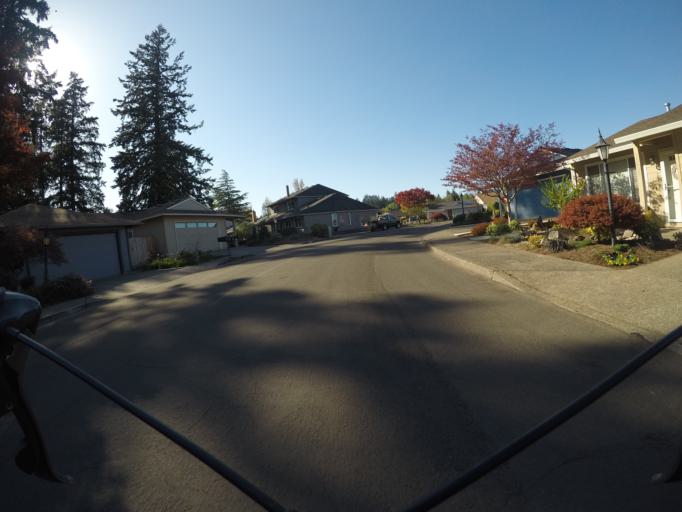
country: US
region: Oregon
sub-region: Washington County
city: Durham
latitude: 45.4071
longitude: -122.7751
